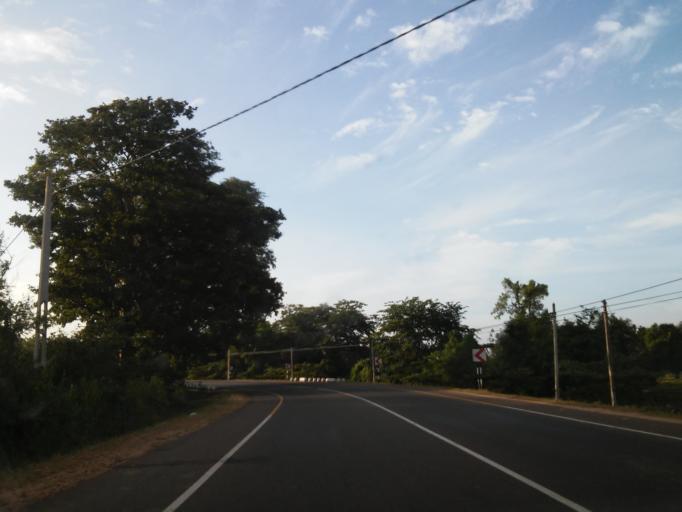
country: LK
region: North Central
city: Anuradhapura
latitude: 8.1337
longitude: 80.5549
